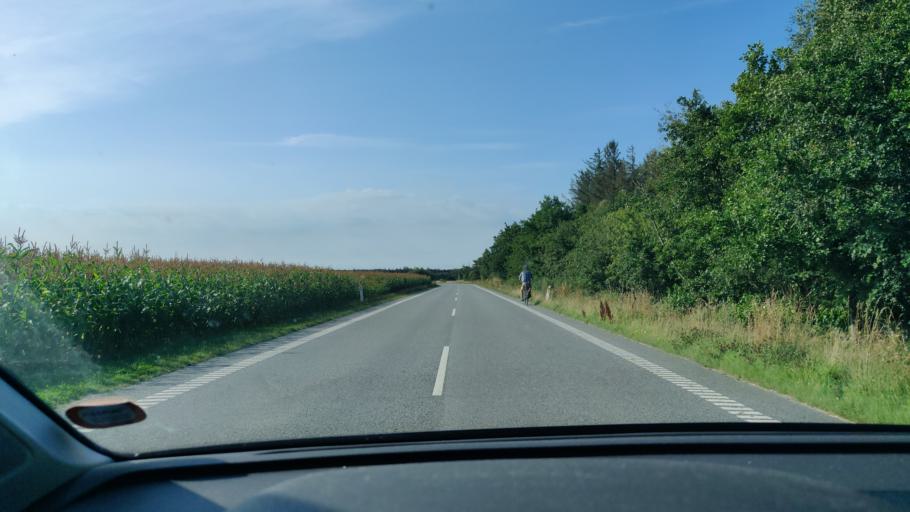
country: DK
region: North Denmark
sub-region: Jammerbugt Kommune
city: Pandrup
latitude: 57.2495
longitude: 9.6457
